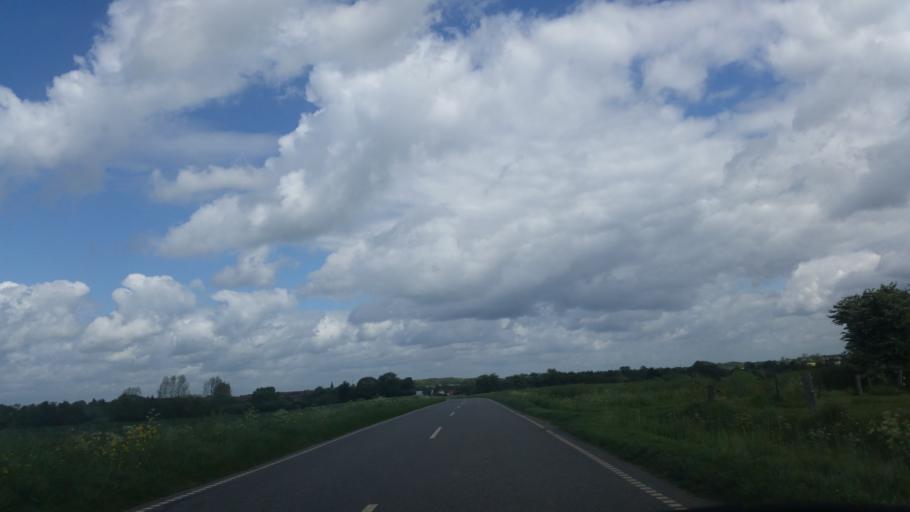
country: DK
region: South Denmark
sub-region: Kolding Kommune
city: Christiansfeld
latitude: 55.3432
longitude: 9.4708
